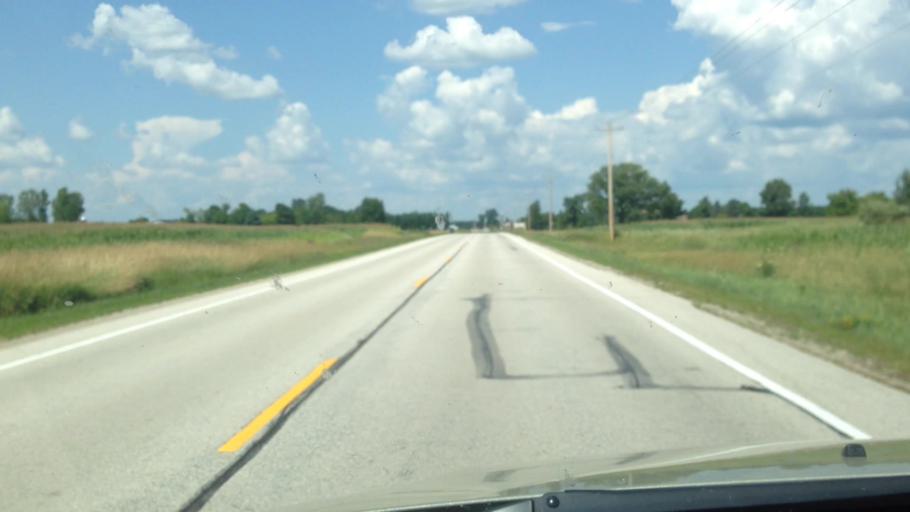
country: US
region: Wisconsin
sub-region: Brown County
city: Pulaski
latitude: 44.6501
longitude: -88.1809
